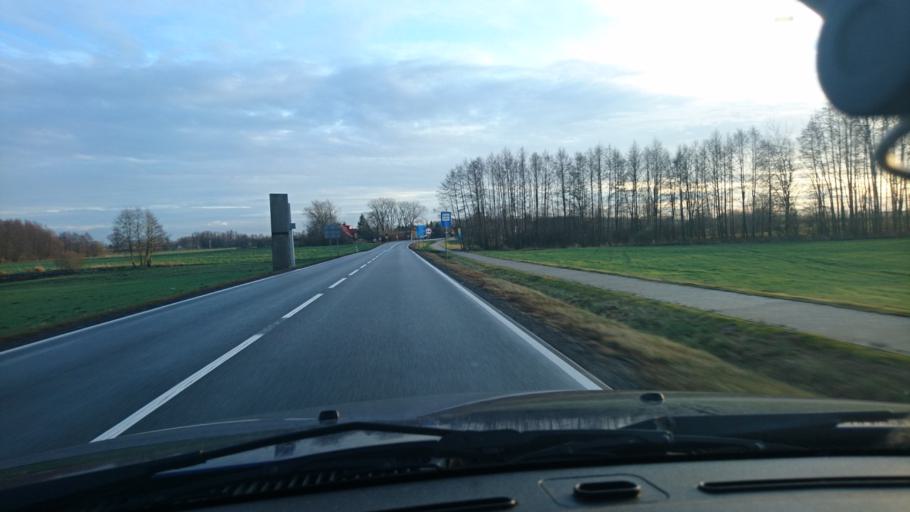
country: PL
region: Greater Poland Voivodeship
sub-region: Powiat kepinski
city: Opatow
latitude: 51.1720
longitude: 18.1459
